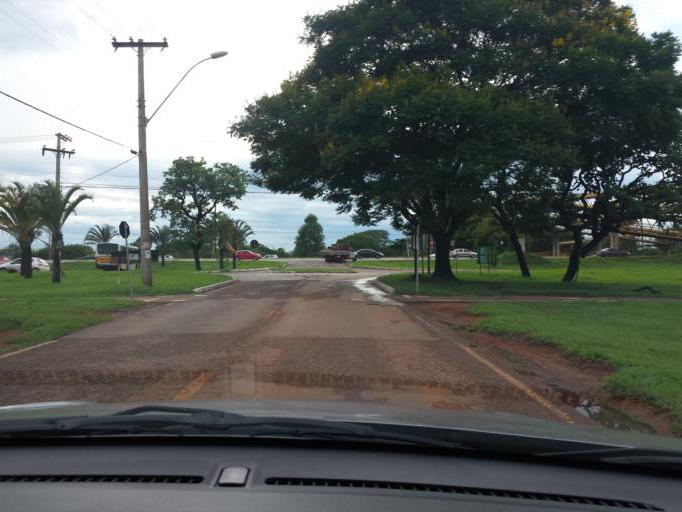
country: BR
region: Federal District
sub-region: Brasilia
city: Brasilia
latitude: -15.9211
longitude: -47.9753
